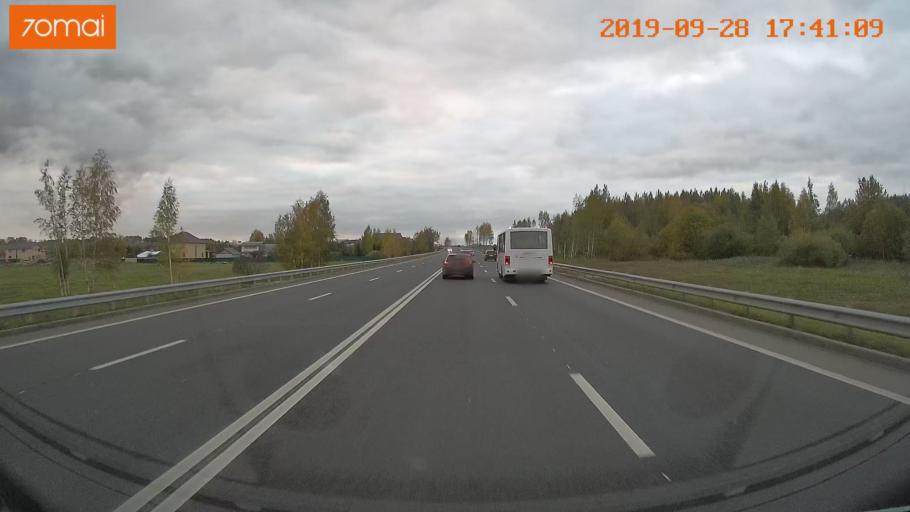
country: RU
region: Jaroslavl
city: Yaroslavl
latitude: 57.5532
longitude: 39.8812
